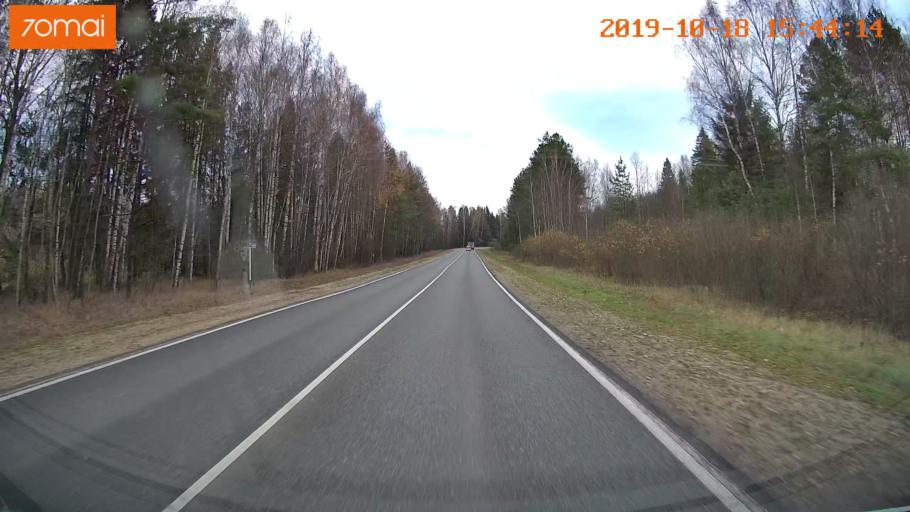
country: RU
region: Vladimir
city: Golovino
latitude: 55.9788
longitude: 40.5475
